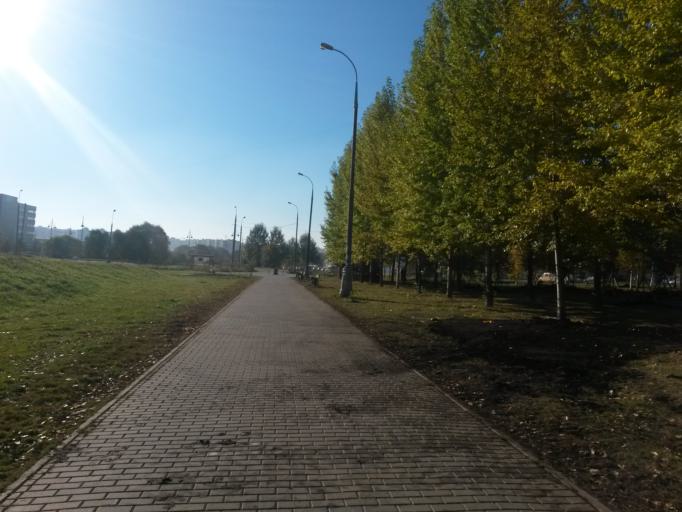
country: RU
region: Moskovskaya
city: Kommunarka
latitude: 55.5427
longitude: 37.5141
